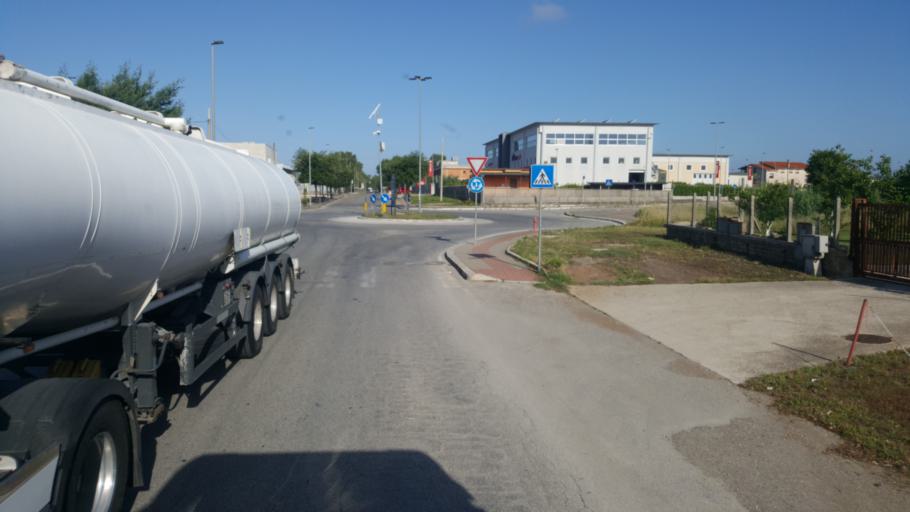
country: IT
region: Latium
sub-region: Provincia di Latina
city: Aprilia
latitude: 41.5785
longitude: 12.6476
